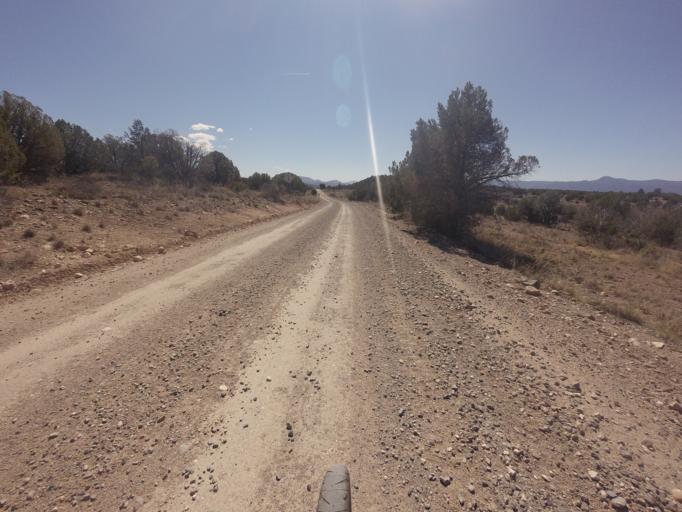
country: US
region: Arizona
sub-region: Yavapai County
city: Lake Montezuma
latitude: 34.5895
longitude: -111.7330
